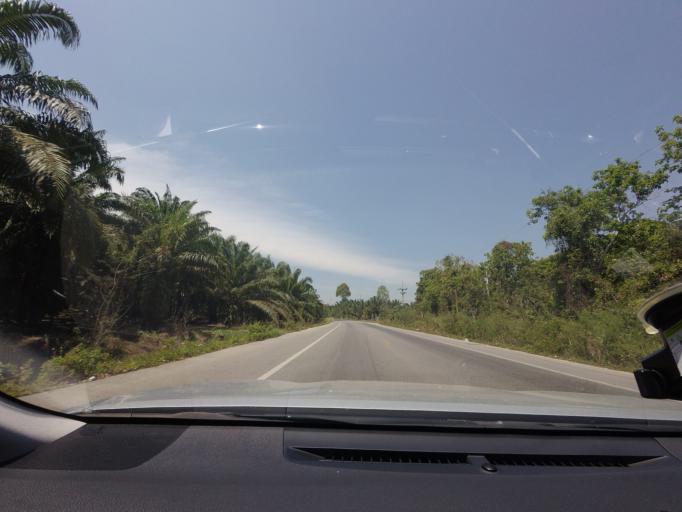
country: TH
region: Surat Thani
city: Tha Chang
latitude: 9.2621
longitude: 99.1785
